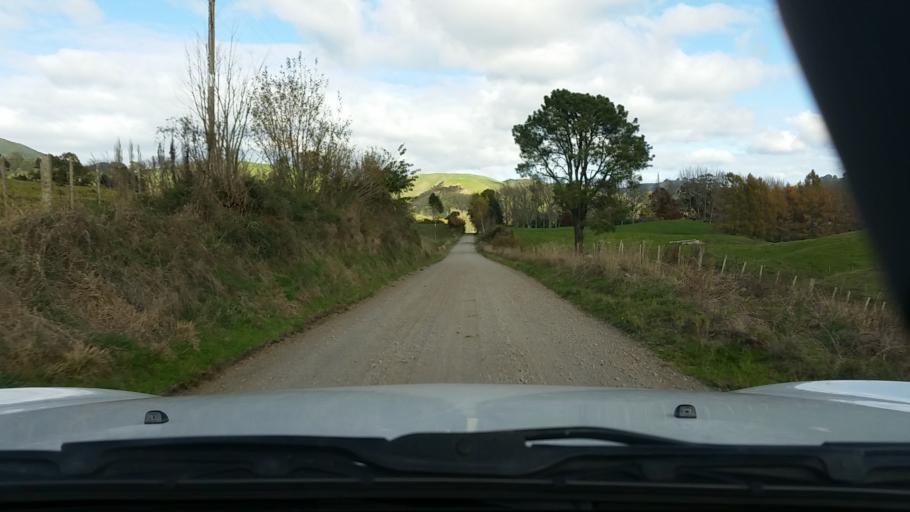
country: NZ
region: Bay of Plenty
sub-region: Rotorua District
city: Rotorua
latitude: -38.3661
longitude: 176.2076
